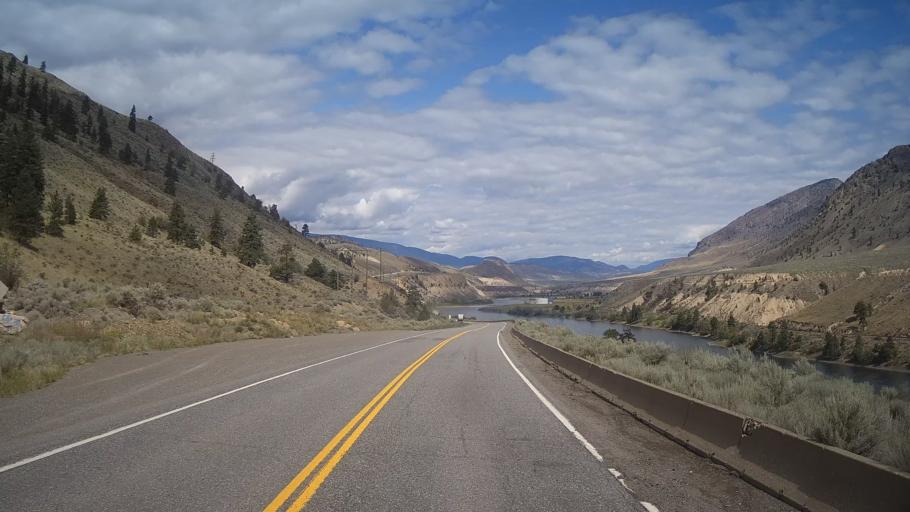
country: CA
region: British Columbia
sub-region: Thompson-Nicola Regional District
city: Ashcroft
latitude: 50.5417
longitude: -121.2895
